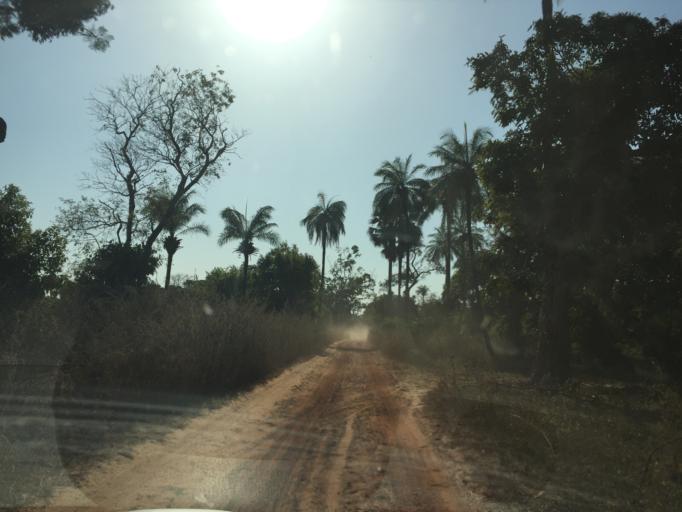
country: GW
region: Oio
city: Farim
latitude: 12.4613
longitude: -15.3006
